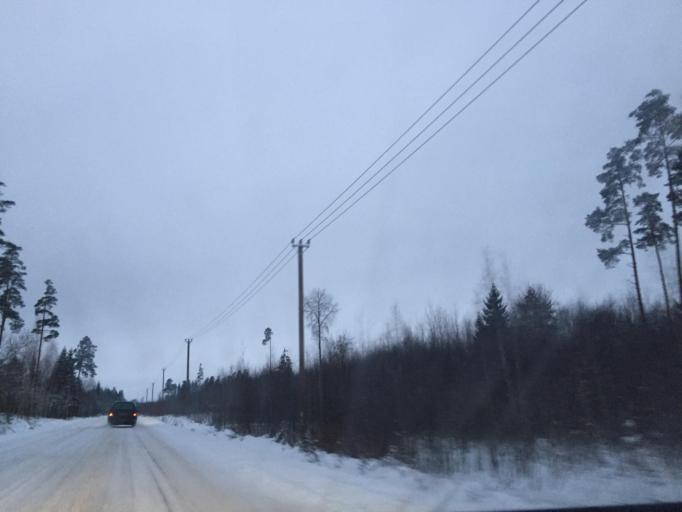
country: LV
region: Raunas
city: Rauna
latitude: 57.4290
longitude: 25.6751
